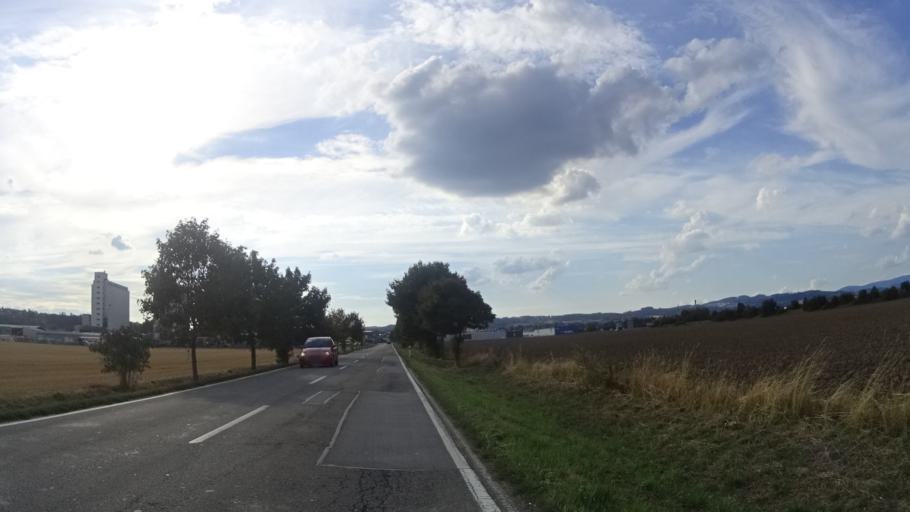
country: CZ
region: Olomoucky
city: Zabreh
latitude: 49.8748
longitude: 16.8985
